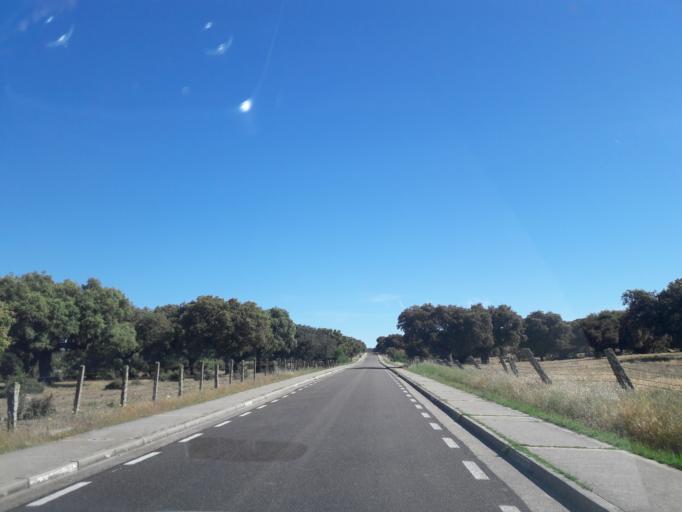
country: ES
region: Castille and Leon
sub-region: Provincia de Salamanca
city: Juzbado
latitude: 41.0744
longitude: -5.8994
